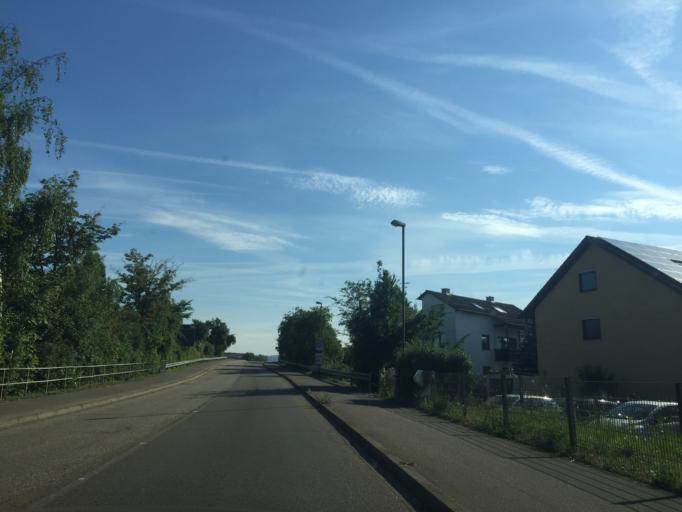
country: DE
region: Baden-Wuerttemberg
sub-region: Karlsruhe Region
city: Eppelheim
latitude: 49.4045
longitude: 8.6354
